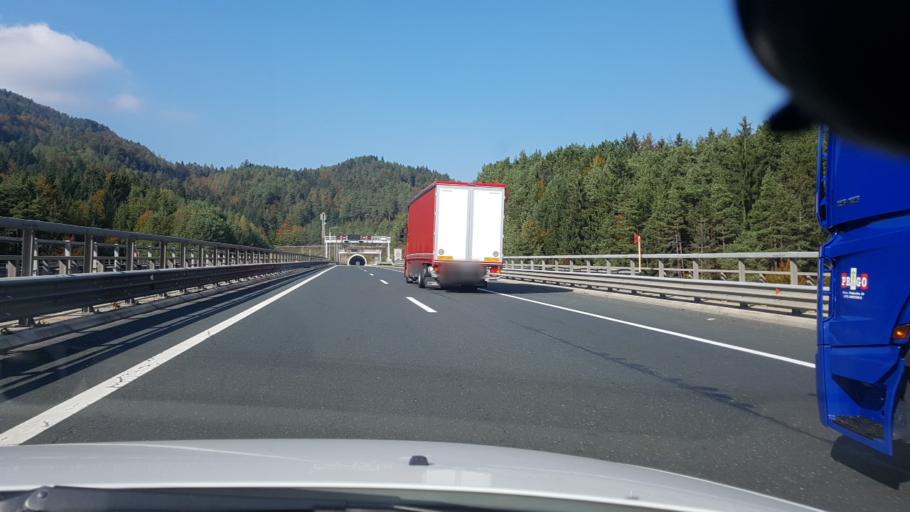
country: AT
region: Carinthia
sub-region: Politischer Bezirk Villach Land
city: Fresach
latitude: 46.6596
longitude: 13.7289
